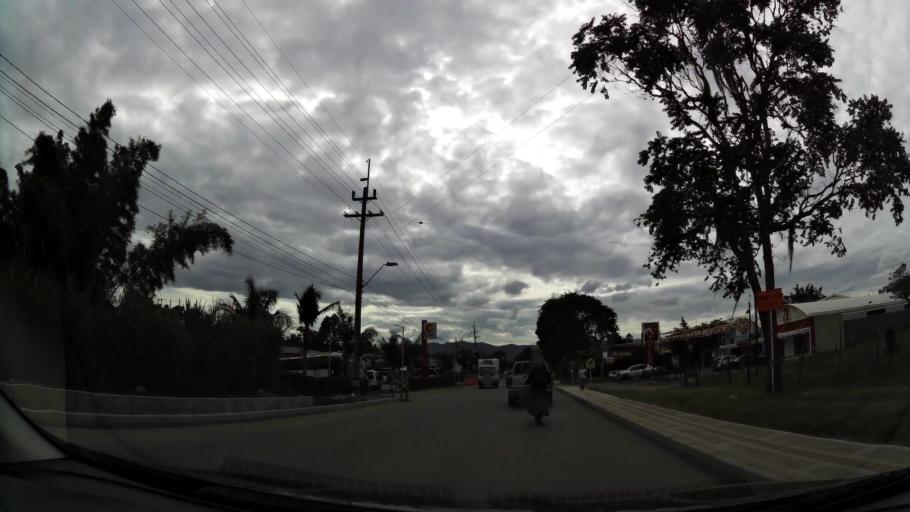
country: CO
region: Antioquia
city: Rionegro
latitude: 6.1529
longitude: -75.4046
